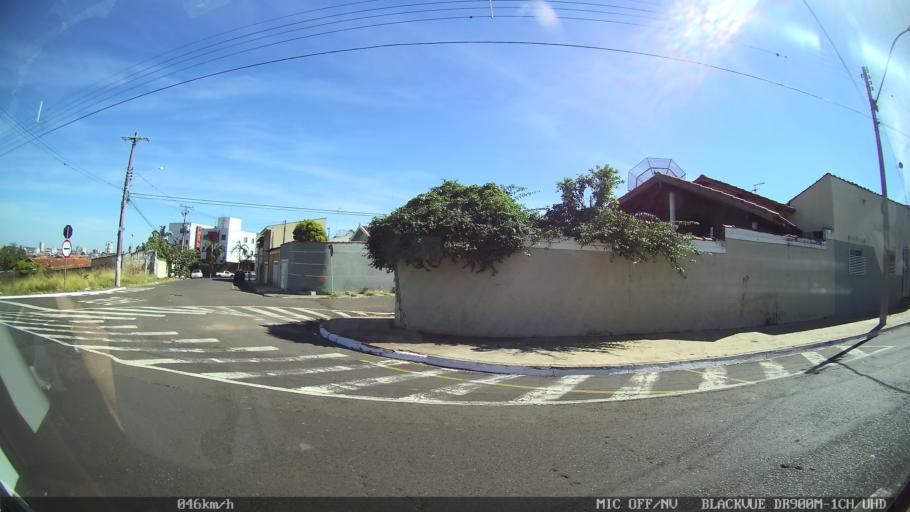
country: BR
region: Sao Paulo
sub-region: Franca
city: Franca
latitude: -20.5277
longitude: -47.3714
